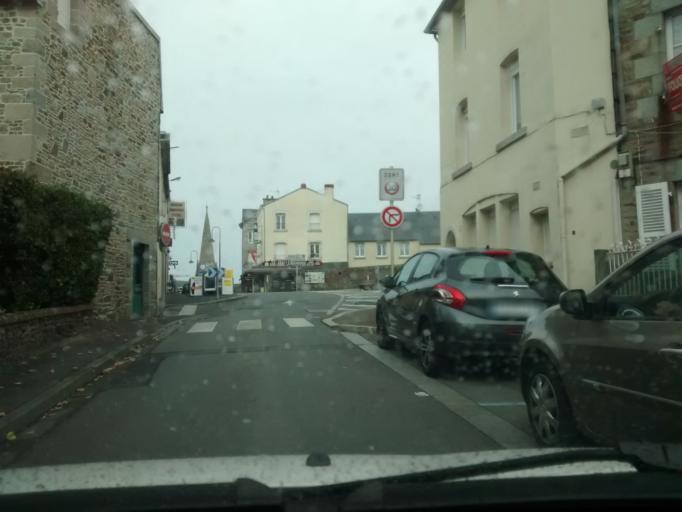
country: FR
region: Lower Normandy
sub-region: Departement de la Manche
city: Saint-Pair-sur-Mer
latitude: 48.8147
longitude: -1.5688
